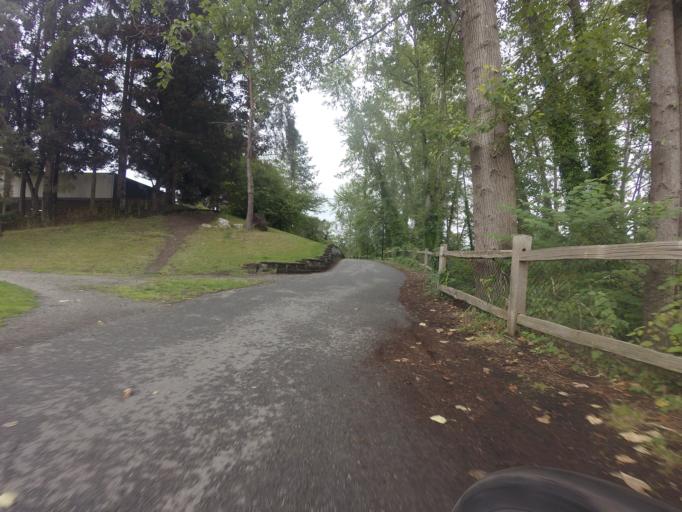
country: CA
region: British Columbia
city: West End
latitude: 49.3237
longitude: -123.1378
